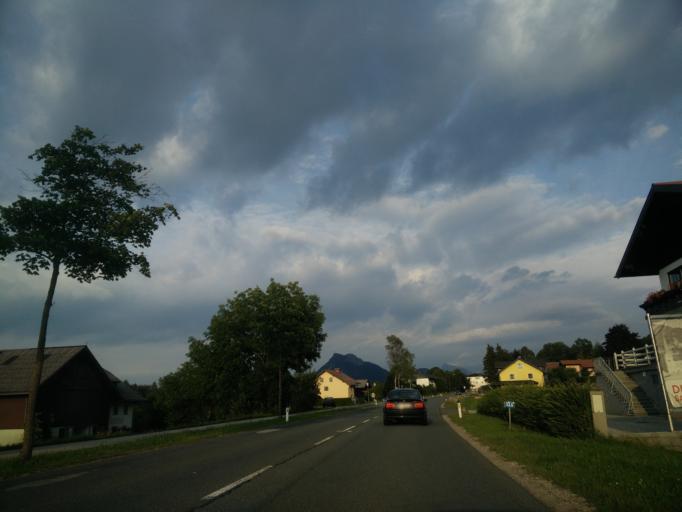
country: AT
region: Salzburg
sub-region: Politischer Bezirk Salzburg-Umgebung
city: Hof bei Salzburg
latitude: 47.8188
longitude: 13.2215
